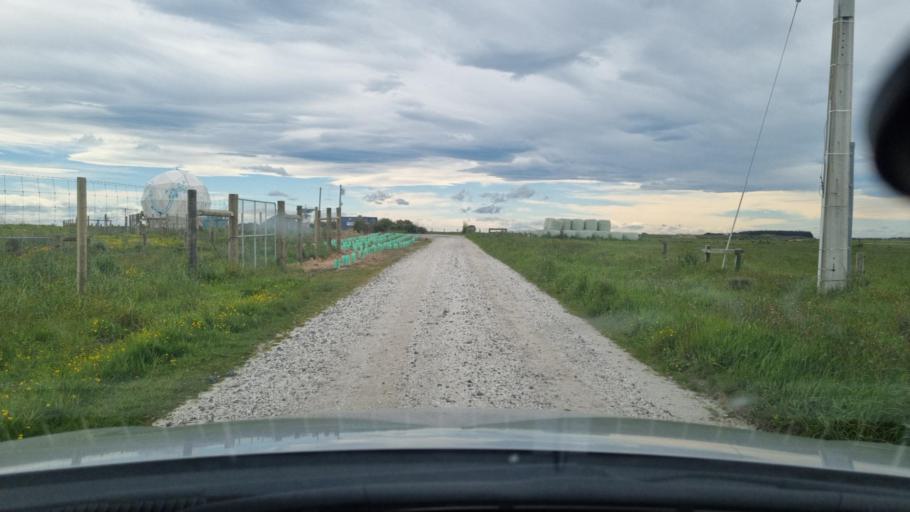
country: NZ
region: Southland
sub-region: Invercargill City
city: Bluff
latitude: -46.5296
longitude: 168.3825
